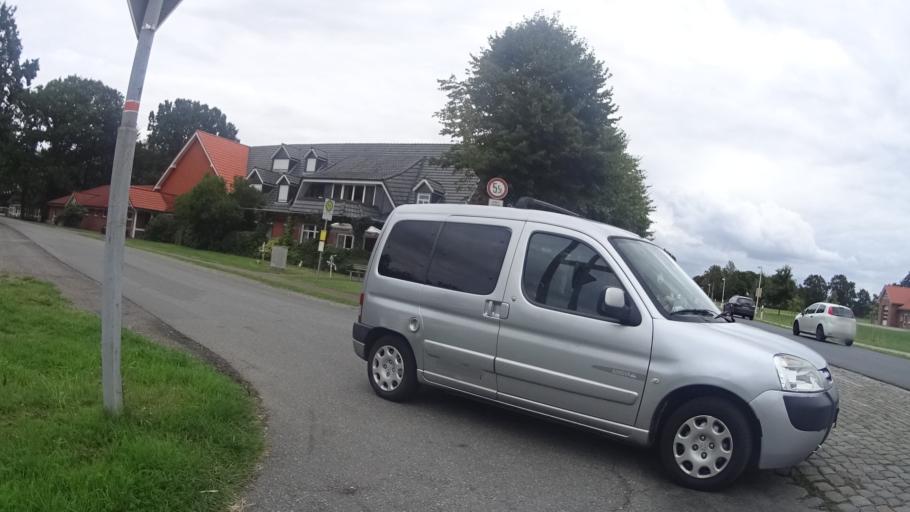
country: DE
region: Lower Saxony
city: Stinstedt
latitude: 53.6352
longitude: 8.9596
